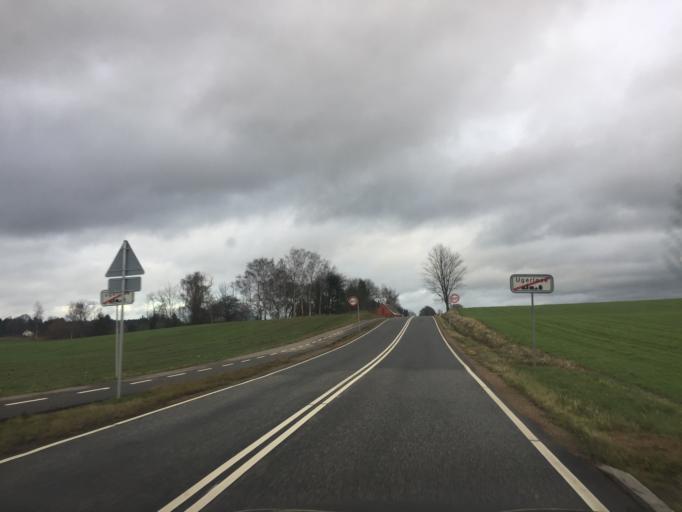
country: DK
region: Zealand
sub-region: Soro Kommune
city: Stenlille
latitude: 55.5892
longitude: 11.6643
